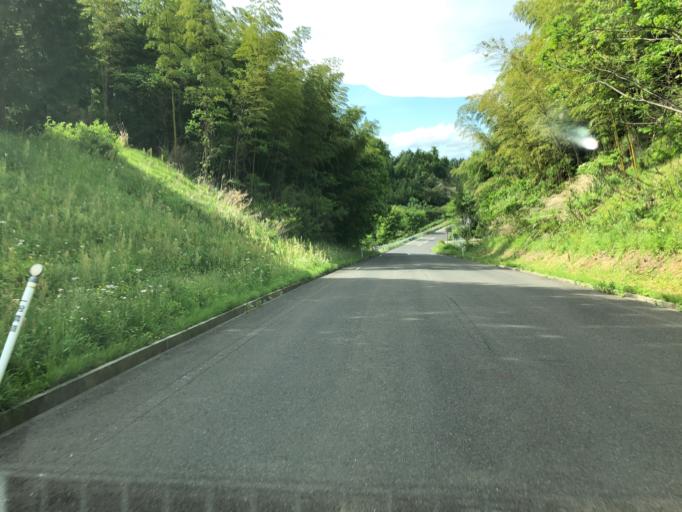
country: JP
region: Fukushima
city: Nihommatsu
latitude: 37.6158
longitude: 140.5246
